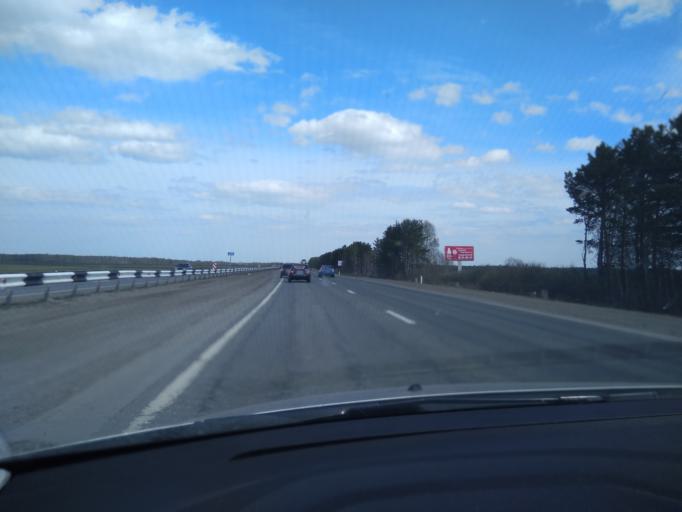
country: RU
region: Tjumen
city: Moskovskiy
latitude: 57.0986
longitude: 65.2931
